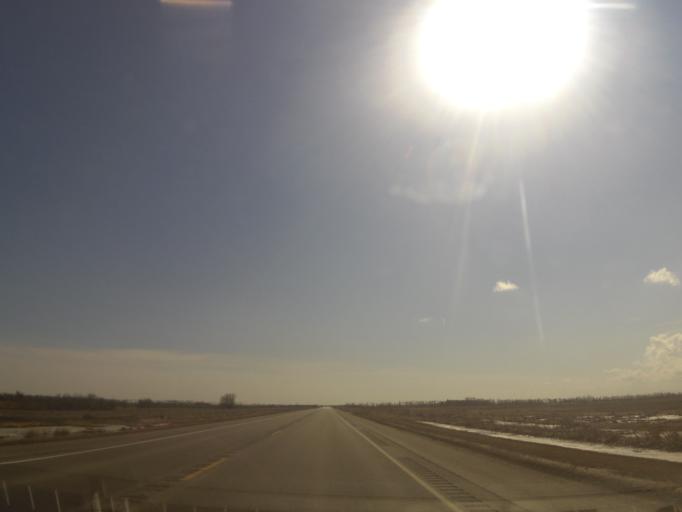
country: US
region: North Dakota
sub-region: Walsh County
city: Grafton
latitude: 48.2549
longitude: -97.3636
